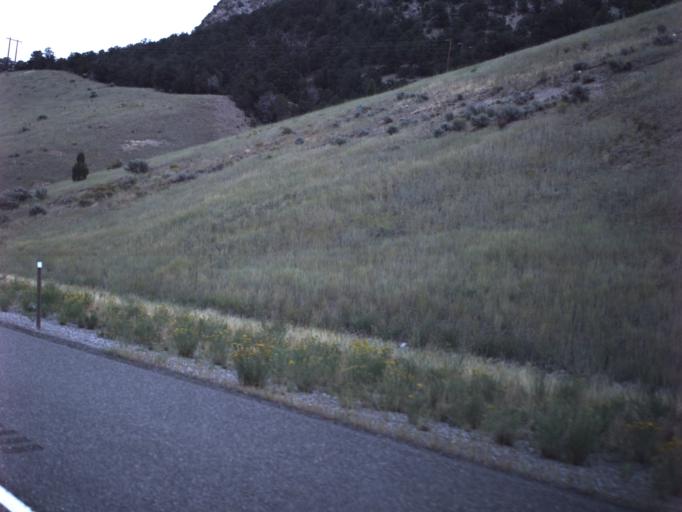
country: US
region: Utah
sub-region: Sevier County
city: Monroe
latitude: 38.5476
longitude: -112.3726
